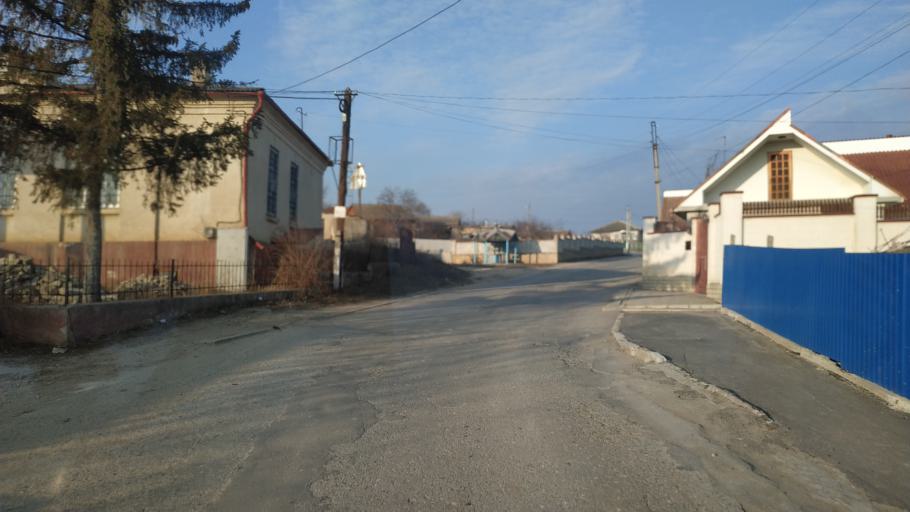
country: MD
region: Hincesti
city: Dancu
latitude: 46.7640
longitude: 28.3592
